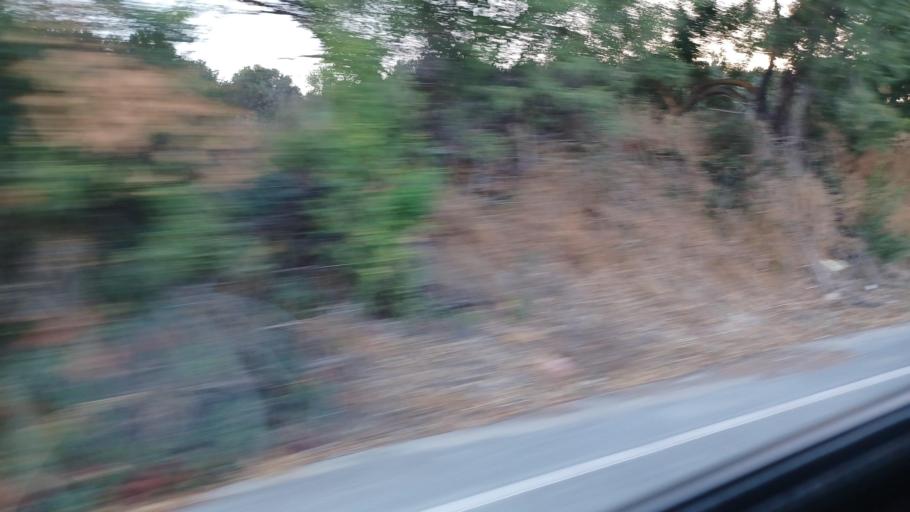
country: CY
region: Pafos
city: Mesogi
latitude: 34.8308
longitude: 32.5659
